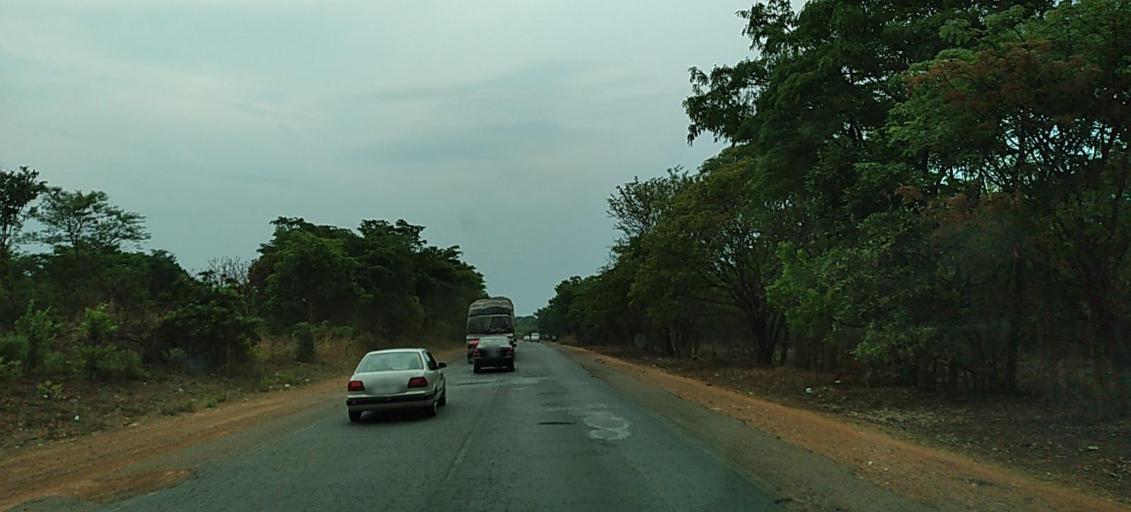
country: ZM
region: Copperbelt
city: Luanshya
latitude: -13.0840
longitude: 28.4411
